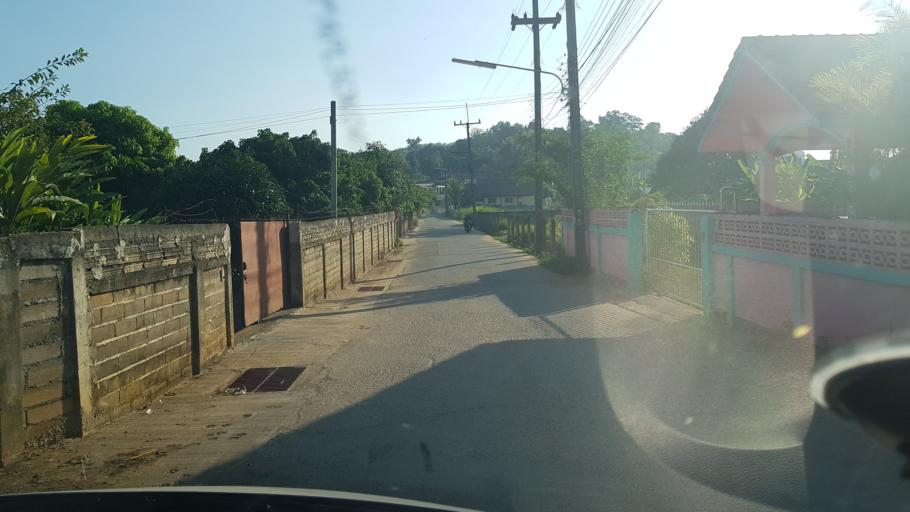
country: TH
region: Chiang Rai
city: Chiang Rai
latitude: 19.9452
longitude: 99.8052
